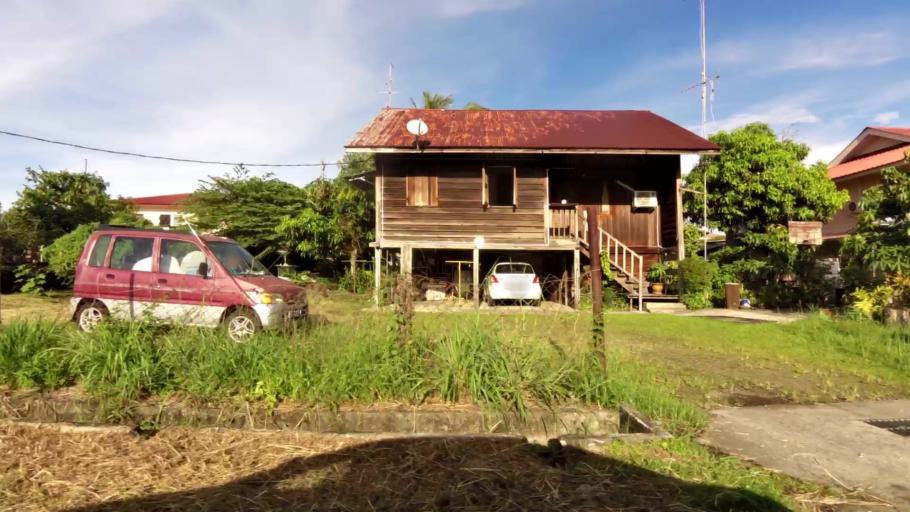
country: BN
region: Belait
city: Kuala Belait
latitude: 4.5842
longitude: 114.1948
